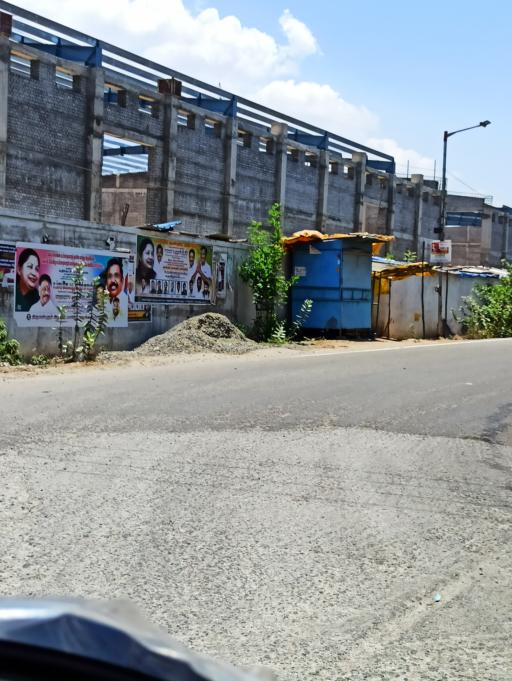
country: IN
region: Tamil Nadu
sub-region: Thiruvallur
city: Chinnasekkadu
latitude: 13.1512
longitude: 80.2410
